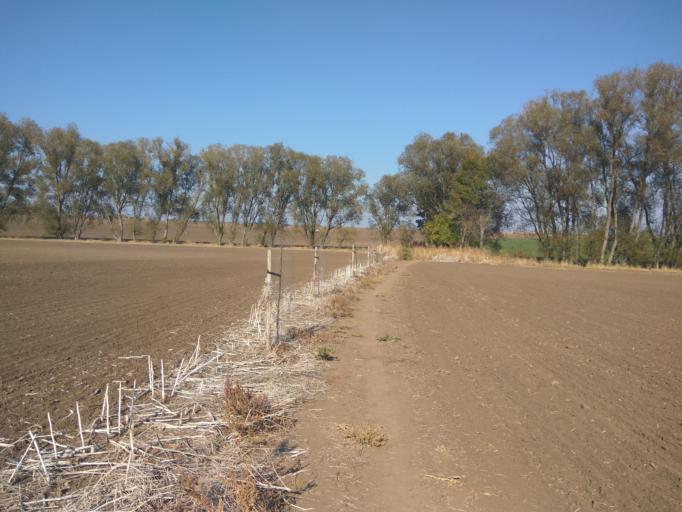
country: CZ
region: Central Bohemia
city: Hovorcovice
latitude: 50.1685
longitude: 14.5282
